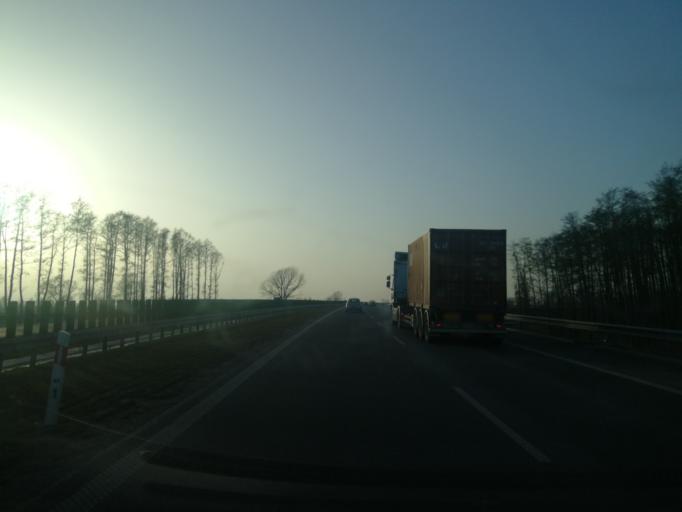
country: PL
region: Warmian-Masurian Voivodeship
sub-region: Powiat elblaski
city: Gronowo Elblaskie
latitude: 54.1646
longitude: 19.2502
